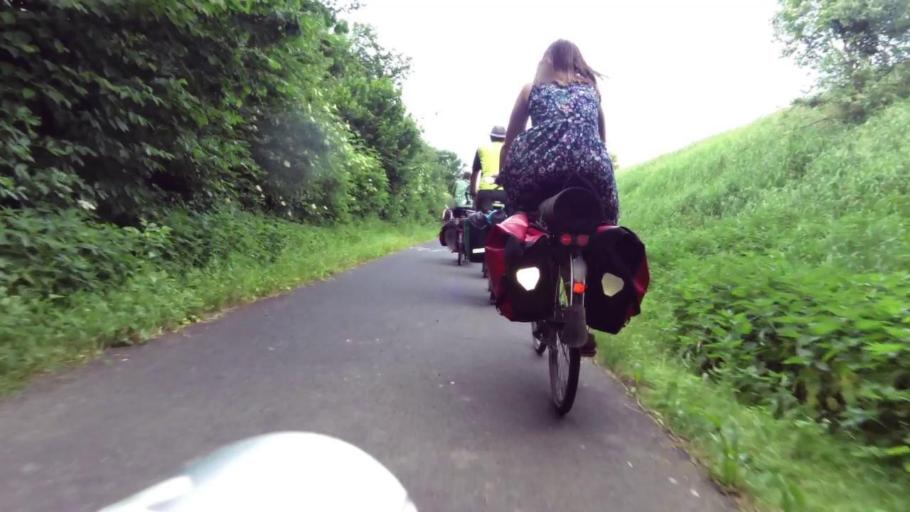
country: PL
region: Kujawsko-Pomorskie
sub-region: Powiat torunski
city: Lubianka
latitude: 53.0921
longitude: 18.5328
